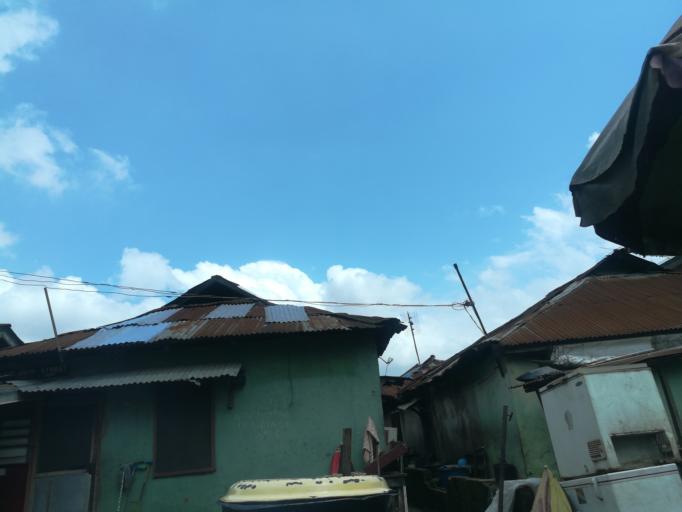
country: NG
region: Lagos
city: Mushin
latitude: 6.5329
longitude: 3.3641
